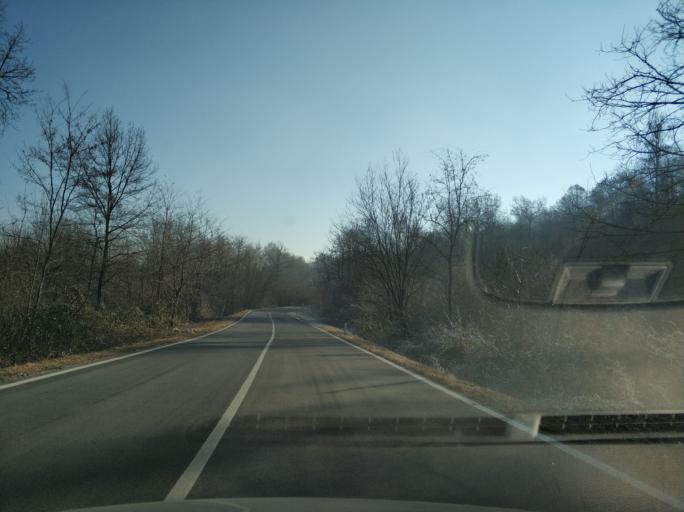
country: IT
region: Piedmont
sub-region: Provincia di Torino
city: Rocca Canavese
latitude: 45.2859
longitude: 7.5836
